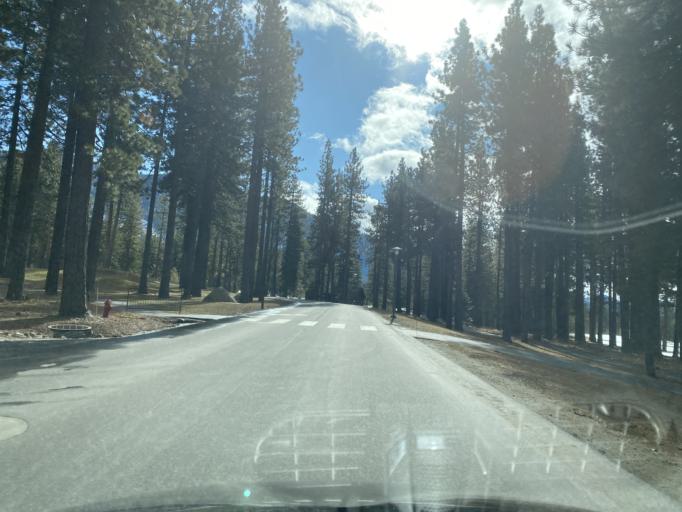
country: US
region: Nevada
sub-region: Douglas County
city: Kingsbury
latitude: 38.9657
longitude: -119.9459
